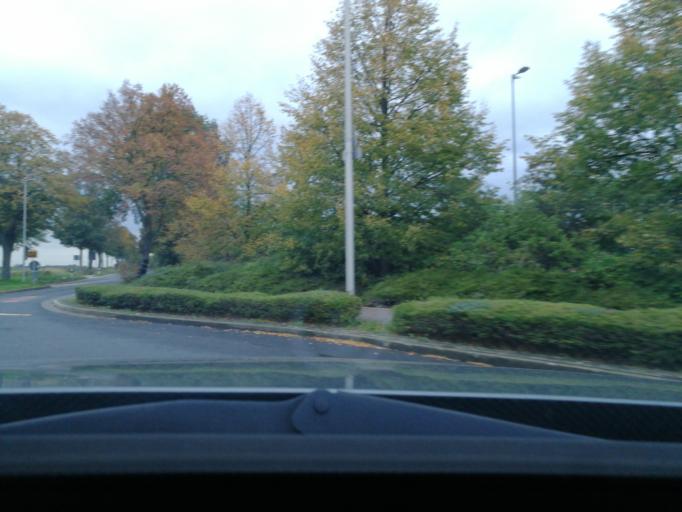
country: DE
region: North Rhine-Westphalia
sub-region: Regierungsbezirk Dusseldorf
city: Dormagen
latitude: 51.1195
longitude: 6.7677
